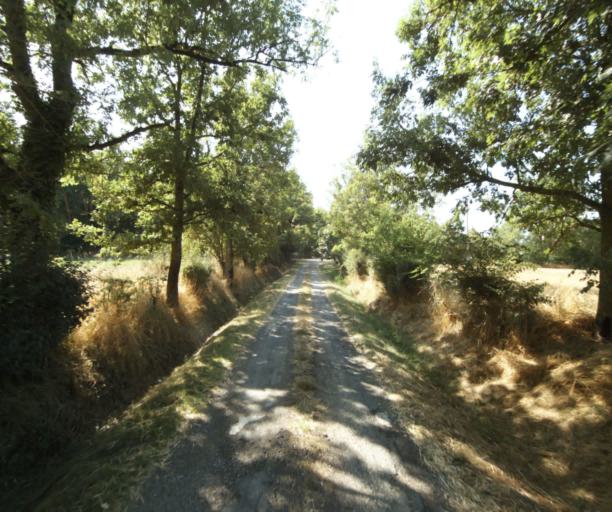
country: FR
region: Midi-Pyrenees
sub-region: Departement de la Haute-Garonne
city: Revel
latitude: 43.5069
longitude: 1.9827
